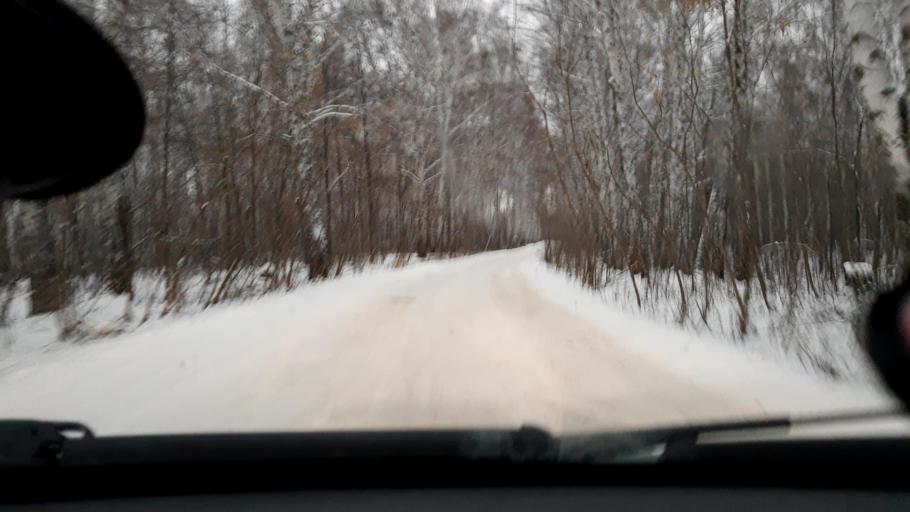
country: RU
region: Bashkortostan
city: Iglino
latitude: 54.8287
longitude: 56.1958
